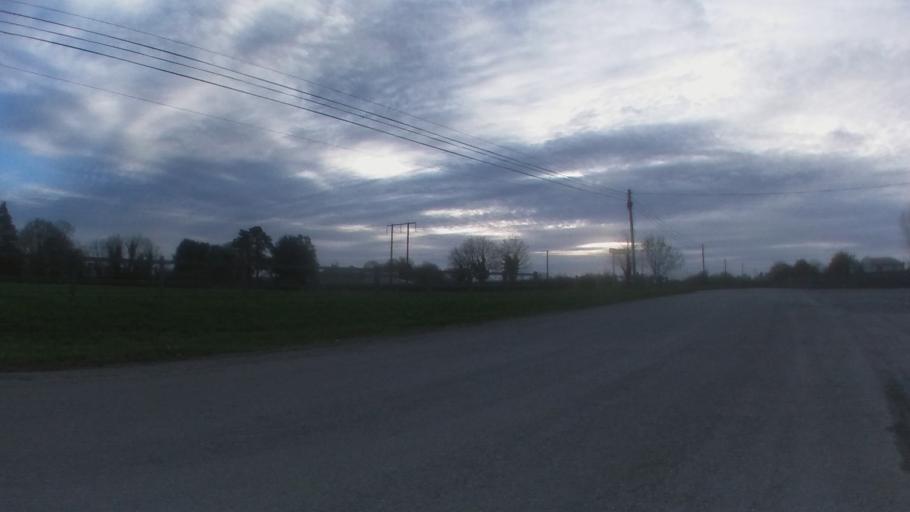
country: IE
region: Leinster
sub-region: Kilkenny
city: Kilkenny
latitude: 52.6778
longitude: -7.1842
